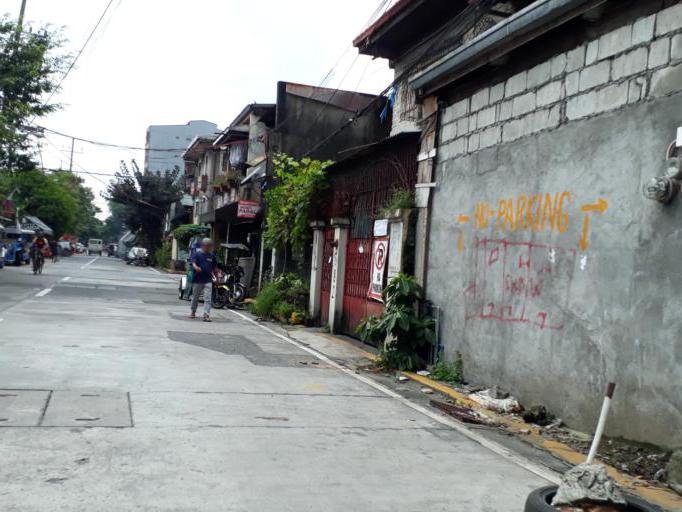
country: PH
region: Metro Manila
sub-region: City of Manila
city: Manila
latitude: 14.6094
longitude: 120.9999
